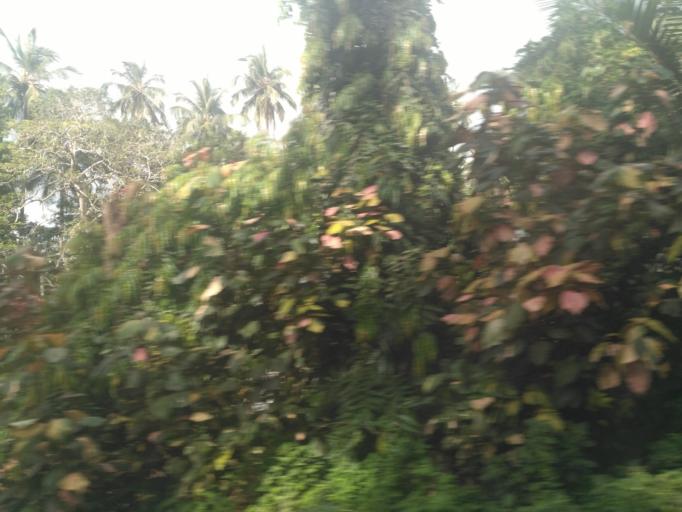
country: TZ
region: Zanzibar Central/South
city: Koani
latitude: -6.1089
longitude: 39.3017
